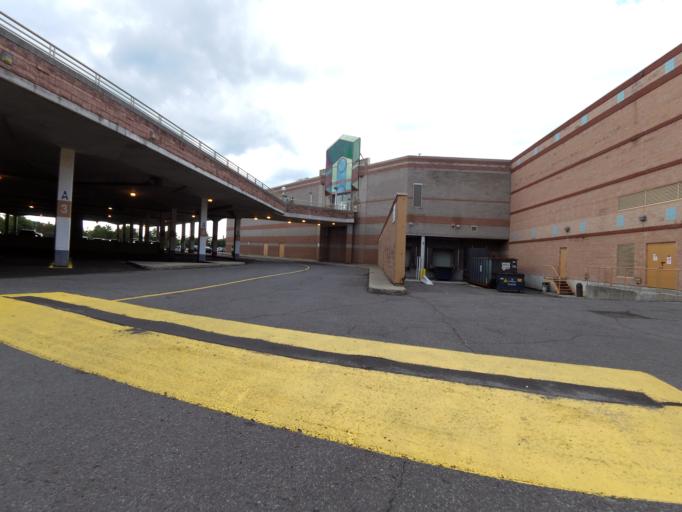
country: CA
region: Quebec
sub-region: Outaouais
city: Gatineau
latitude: 45.4771
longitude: -75.5177
